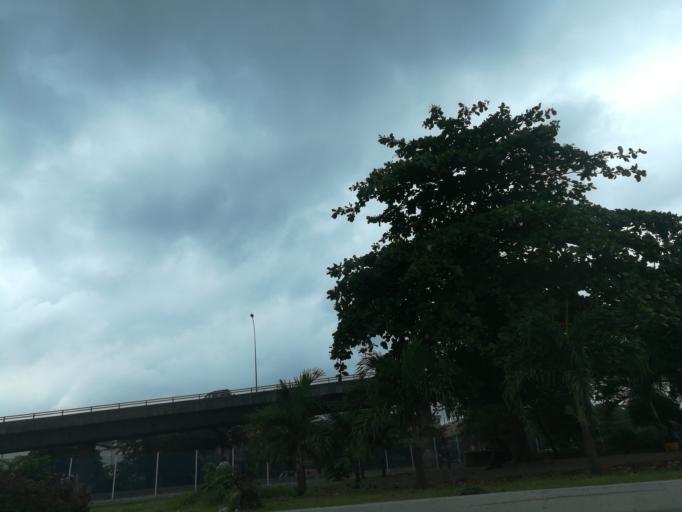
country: NG
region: Lagos
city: Oshodi
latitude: 6.5492
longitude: 3.3380
